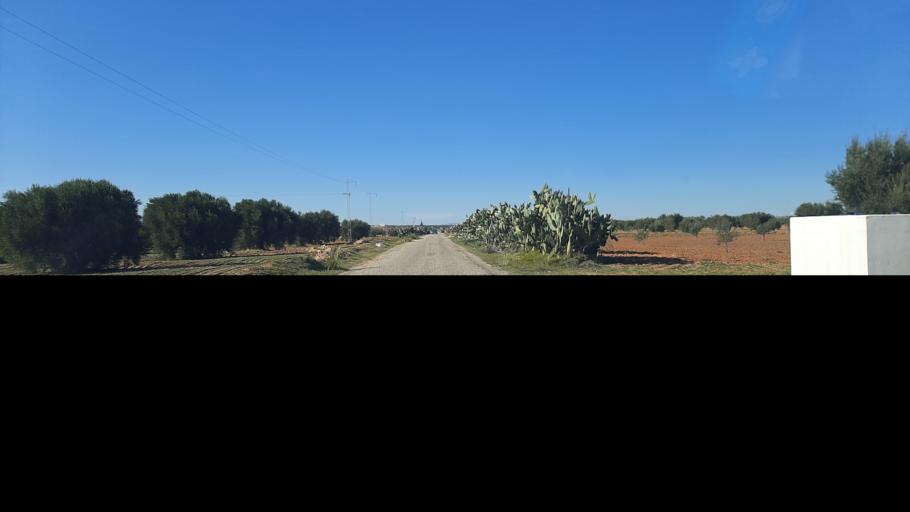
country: TN
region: Safaqis
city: Bi'r `Ali Bin Khalifah
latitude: 35.0131
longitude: 10.0789
